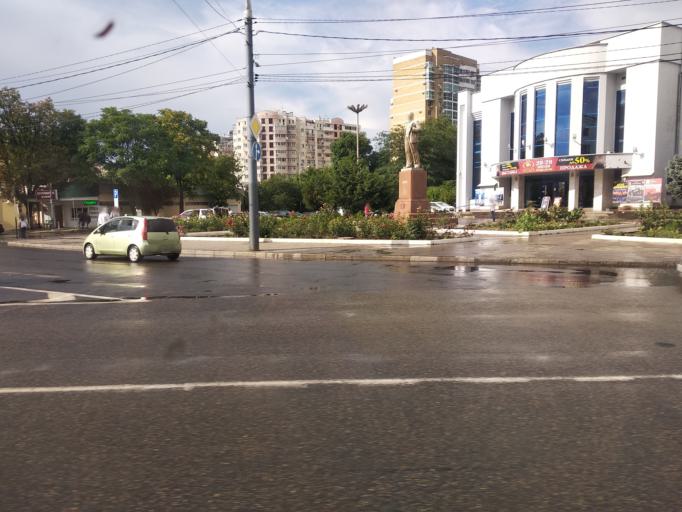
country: RU
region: Krasnodarskiy
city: Krasnodar
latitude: 45.0190
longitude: 38.9850
